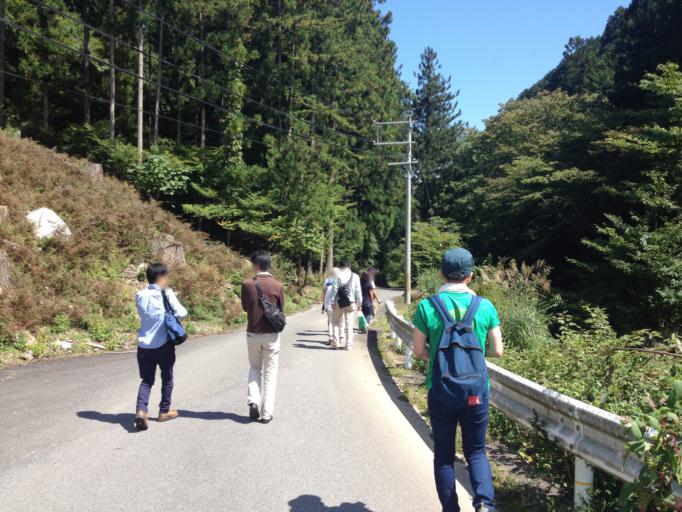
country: JP
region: Nara
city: Yoshino-cho
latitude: 34.3162
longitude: 135.9329
